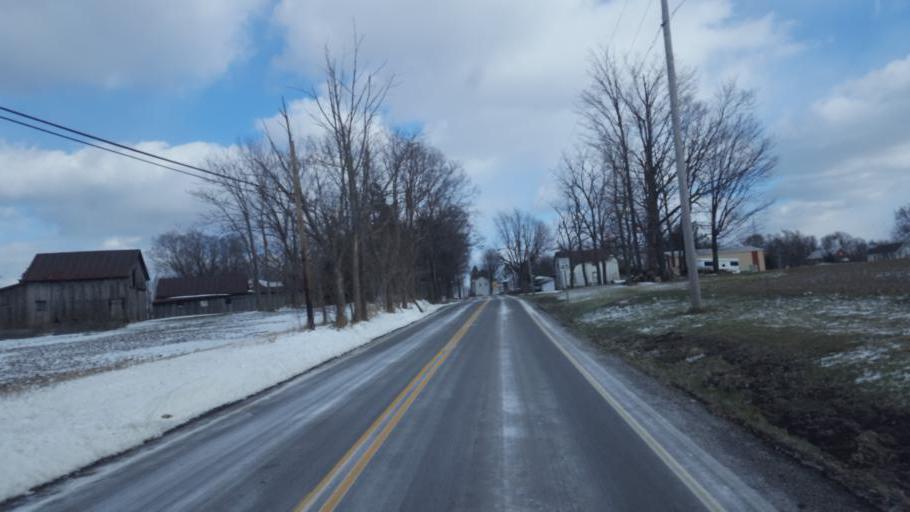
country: US
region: Ohio
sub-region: Crawford County
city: Galion
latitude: 40.7091
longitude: -82.7192
